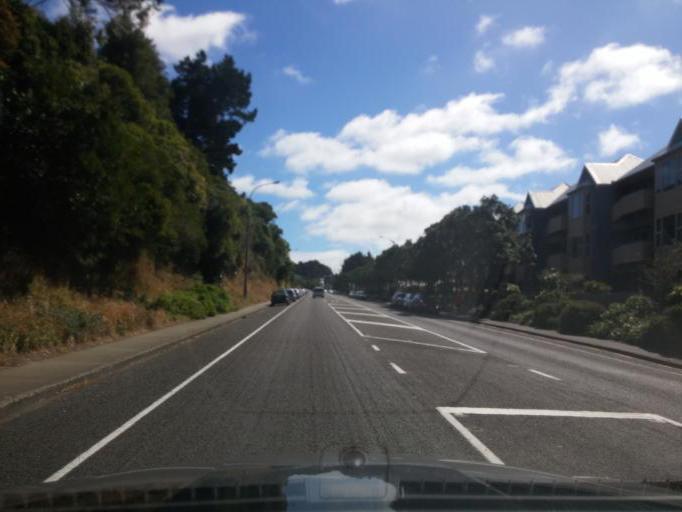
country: NZ
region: Wellington
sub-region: Wellington City
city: Wellington
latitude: -41.2351
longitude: 174.7981
